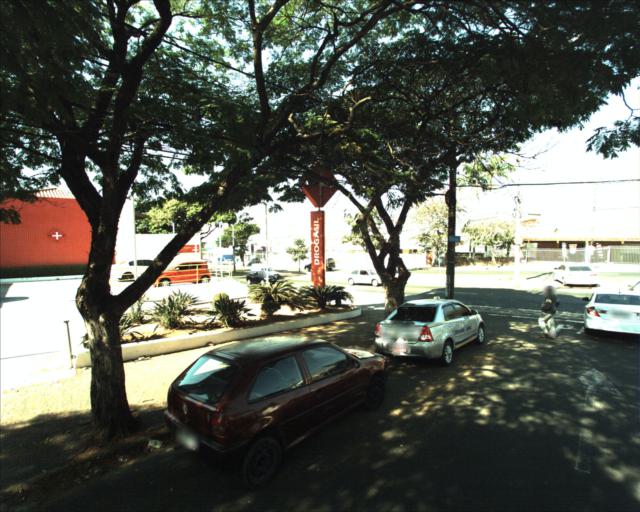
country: BR
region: Sao Paulo
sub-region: Sorocaba
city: Sorocaba
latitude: -23.4930
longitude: -47.4671
